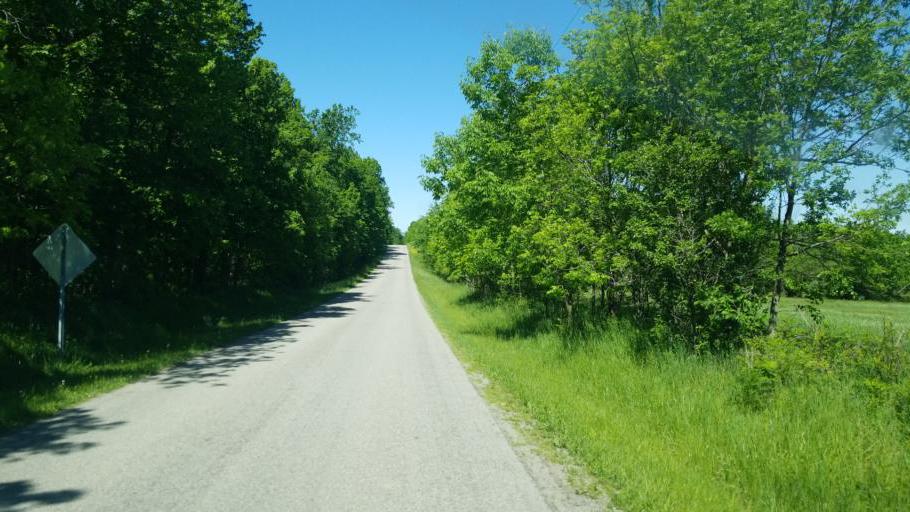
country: US
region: Ohio
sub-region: Logan County
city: Northwood
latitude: 40.4377
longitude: -83.7194
